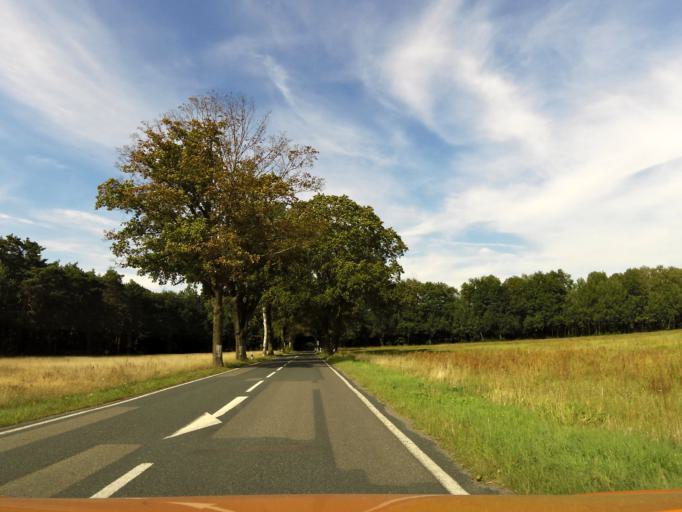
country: DE
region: Brandenburg
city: Michendorf
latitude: 52.2845
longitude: 13.1138
